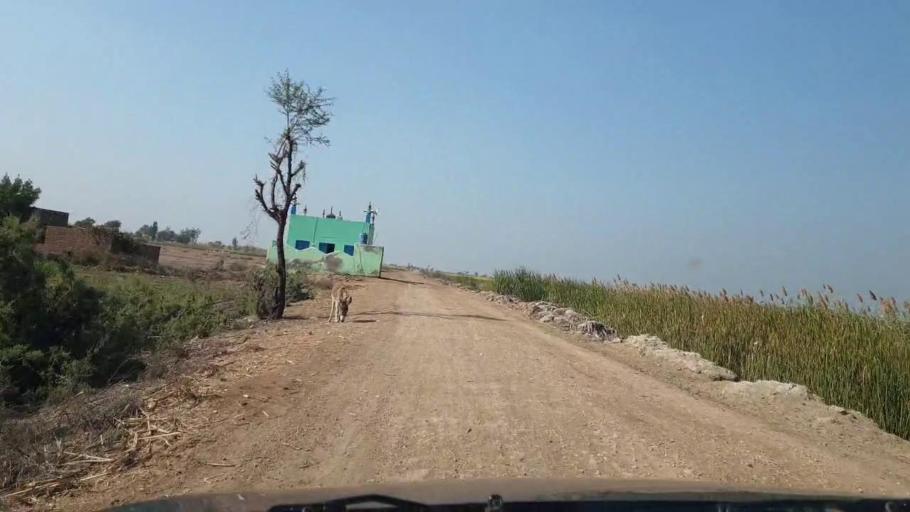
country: PK
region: Sindh
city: Sinjhoro
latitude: 26.0460
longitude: 68.7507
